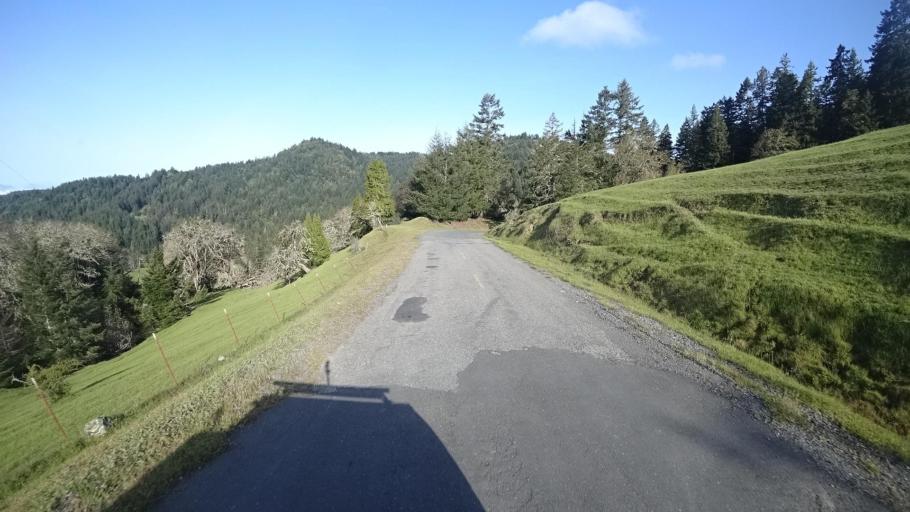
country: US
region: California
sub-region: Humboldt County
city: Bayside
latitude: 40.6909
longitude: -123.9396
